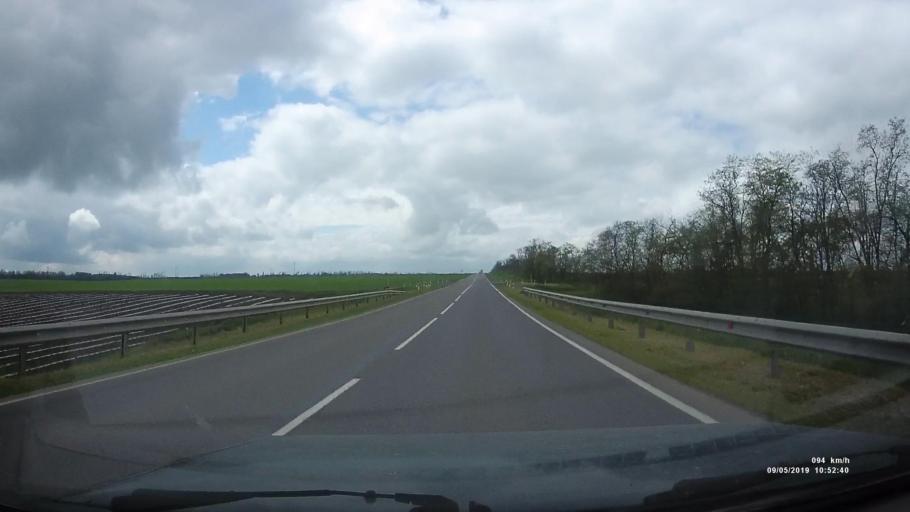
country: RU
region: Rostov
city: Peshkovo
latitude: 46.8980
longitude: 39.3508
